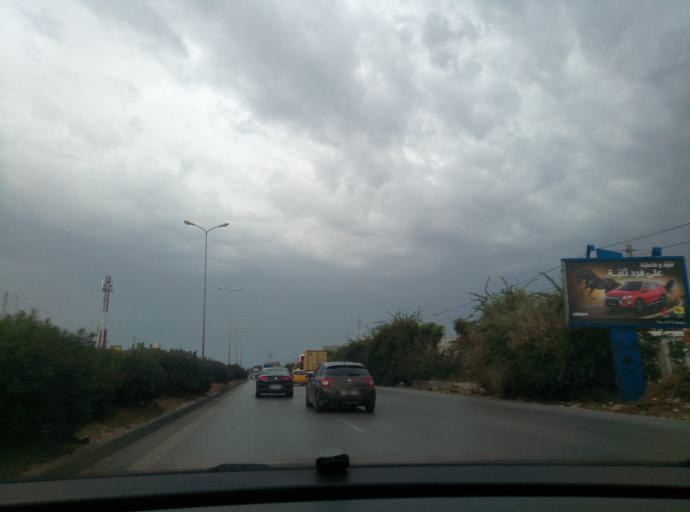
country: TN
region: Bin 'Arus
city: Ben Arous
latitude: 36.7530
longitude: 10.2037
